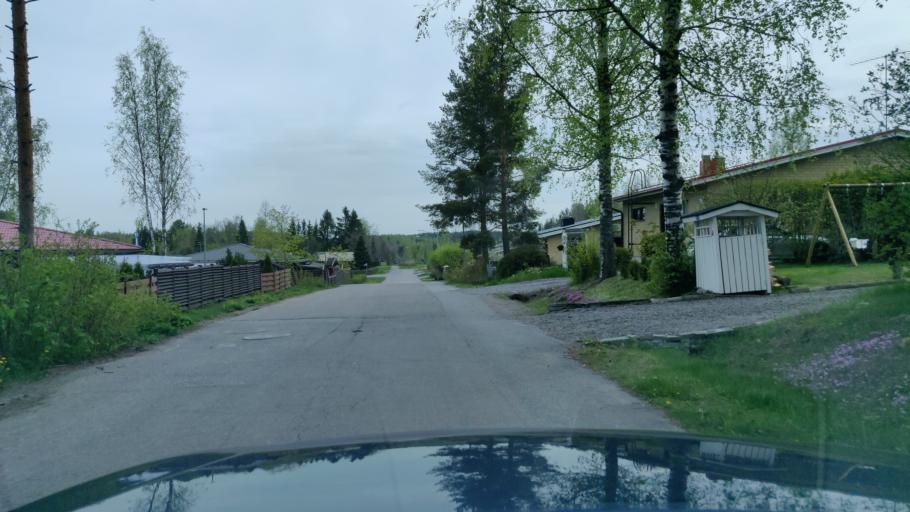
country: FI
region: Uusimaa
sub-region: Helsinki
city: Nurmijaervi
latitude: 60.3679
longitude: 24.7456
